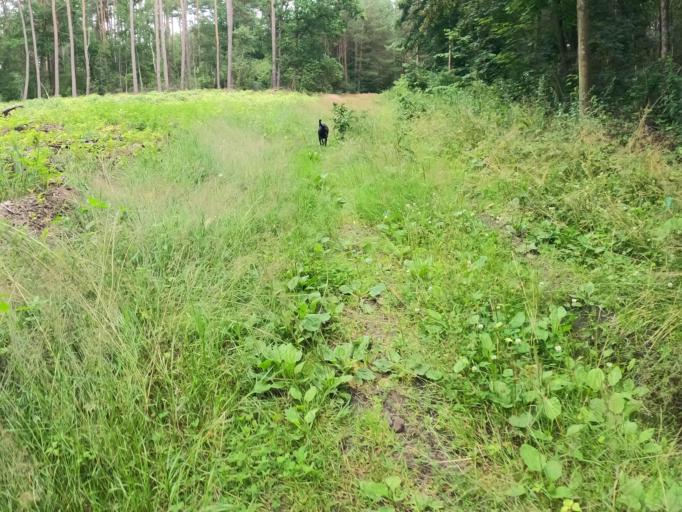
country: PL
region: West Pomeranian Voivodeship
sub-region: Powiat bialogardzki
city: Karlino
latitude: 53.9979
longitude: 15.9054
